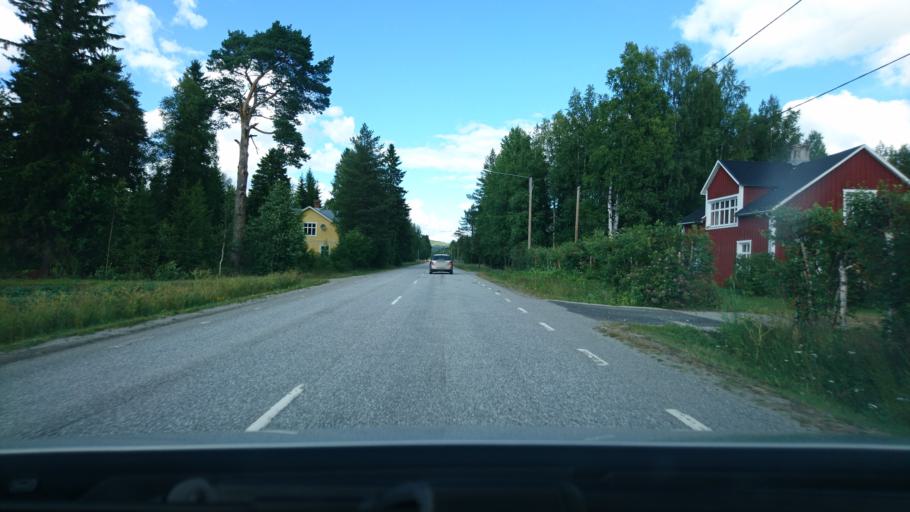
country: SE
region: Vaesterbotten
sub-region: Asele Kommun
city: Asele
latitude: 64.0122
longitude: 17.2907
